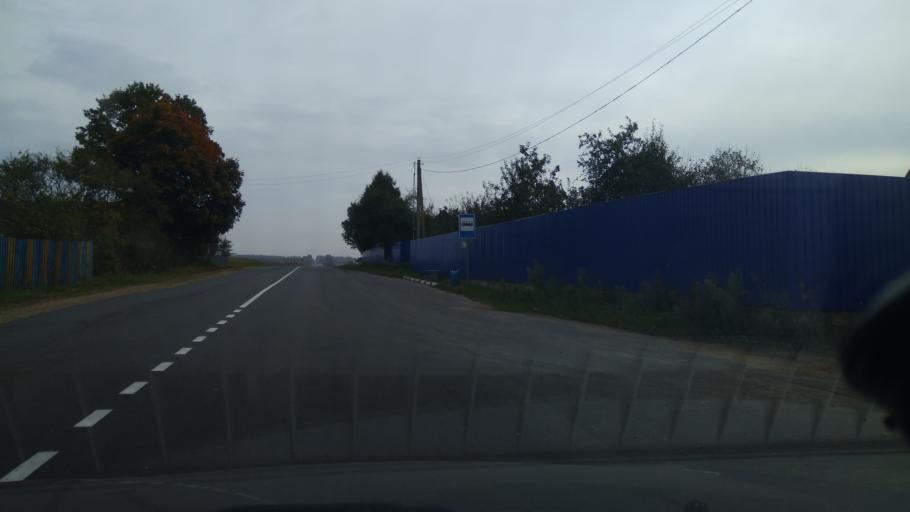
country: BY
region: Minsk
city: Rudzyensk
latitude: 53.6157
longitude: 27.7405
